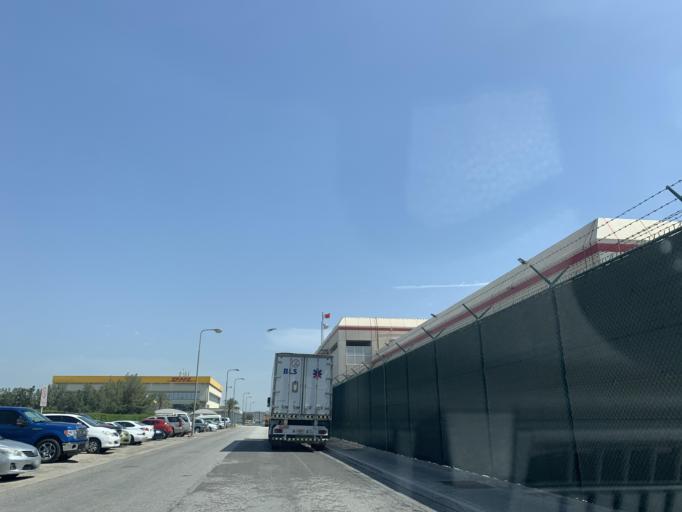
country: BH
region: Muharraq
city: Al Muharraq
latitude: 26.2702
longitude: 50.6209
